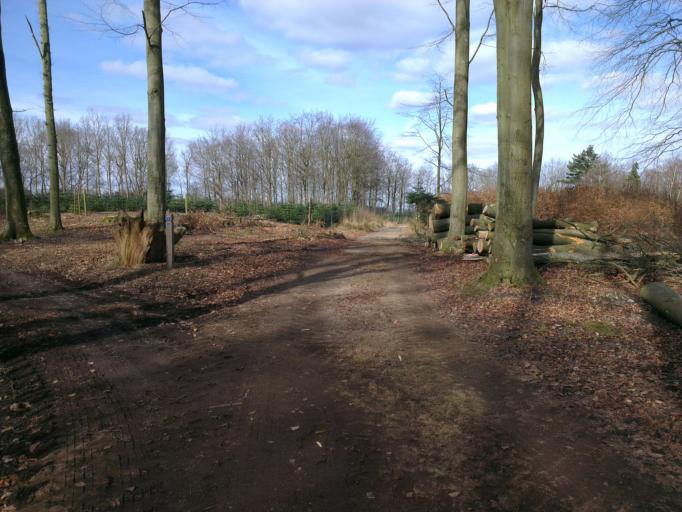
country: DK
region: Zealand
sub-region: Roskilde Kommune
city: Jyllinge
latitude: 55.7452
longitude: 12.0585
